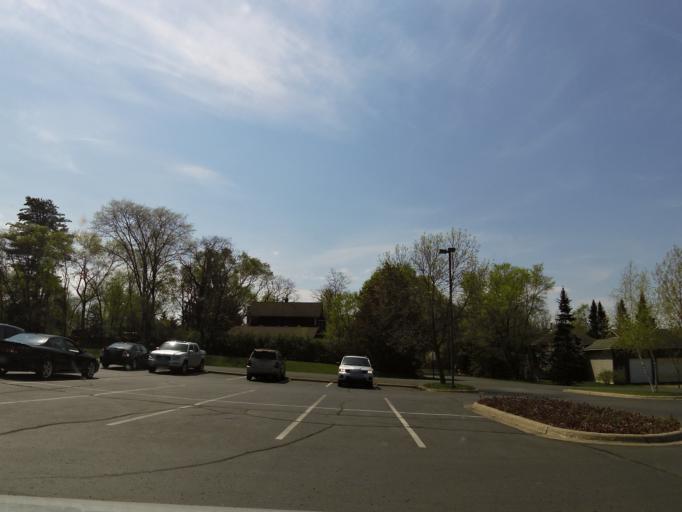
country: US
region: Minnesota
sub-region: Washington County
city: Lake Saint Croix Beach
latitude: 44.9296
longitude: -92.7675
